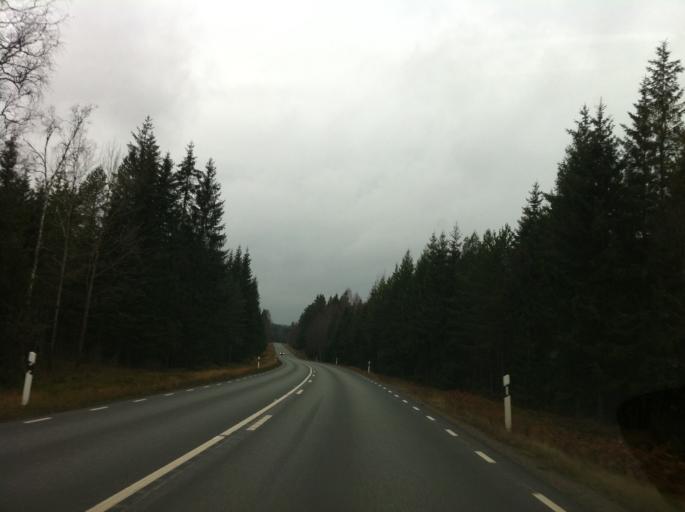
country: SE
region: Joenkoeping
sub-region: Savsjo Kommun
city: Saevsjoe
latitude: 57.3923
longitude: 14.7397
